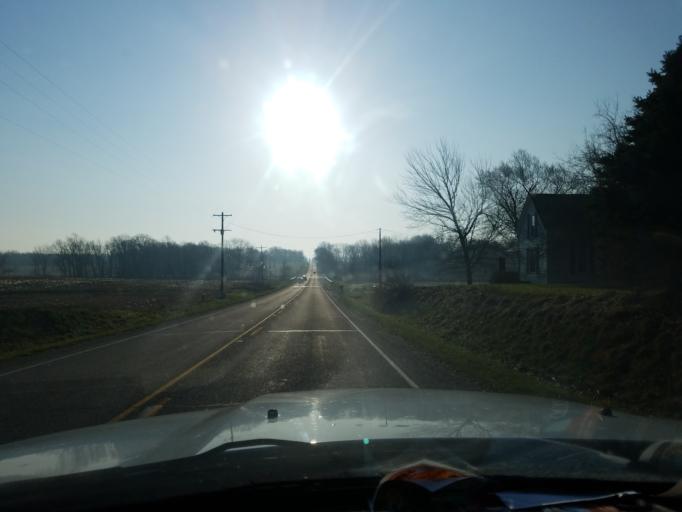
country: US
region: Indiana
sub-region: Vigo County
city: Seelyville
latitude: 39.3899
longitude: -87.2343
